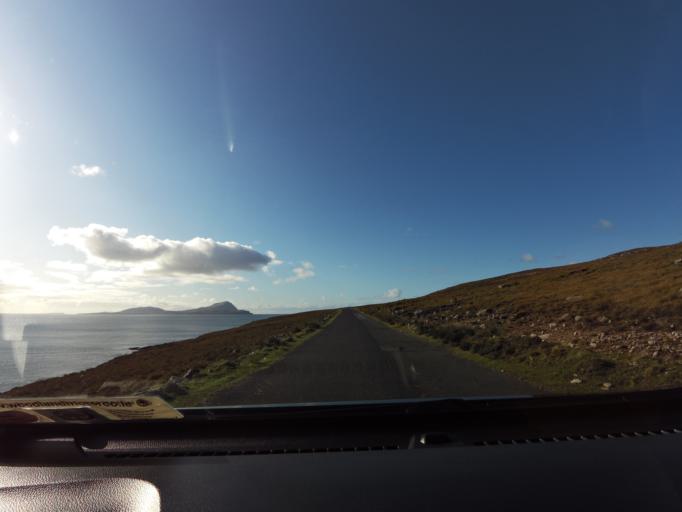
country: IE
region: Connaught
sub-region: Maigh Eo
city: Westport
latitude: 53.8682
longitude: -9.8592
